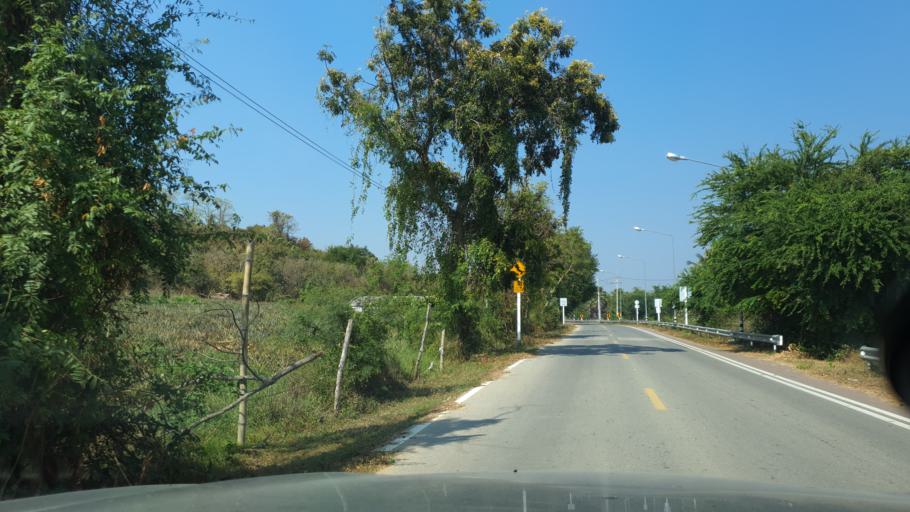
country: TH
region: Prachuap Khiri Khan
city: Sam Roi Yot
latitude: 12.2825
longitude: 99.9728
